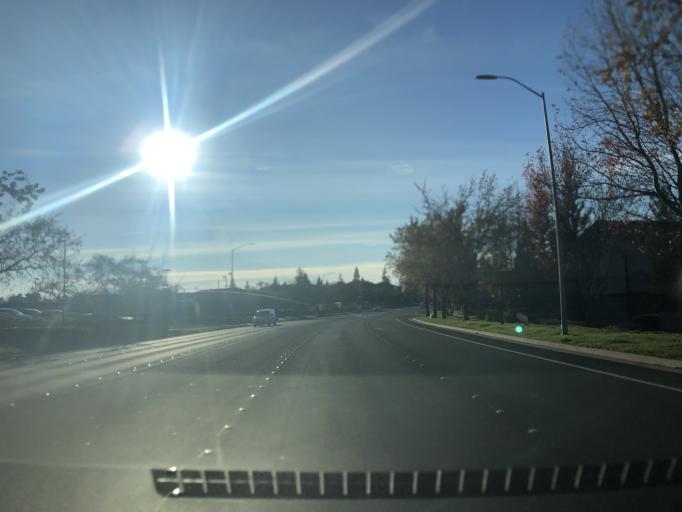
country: US
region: California
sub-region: Placer County
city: Roseville
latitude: 38.7601
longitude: -121.2960
